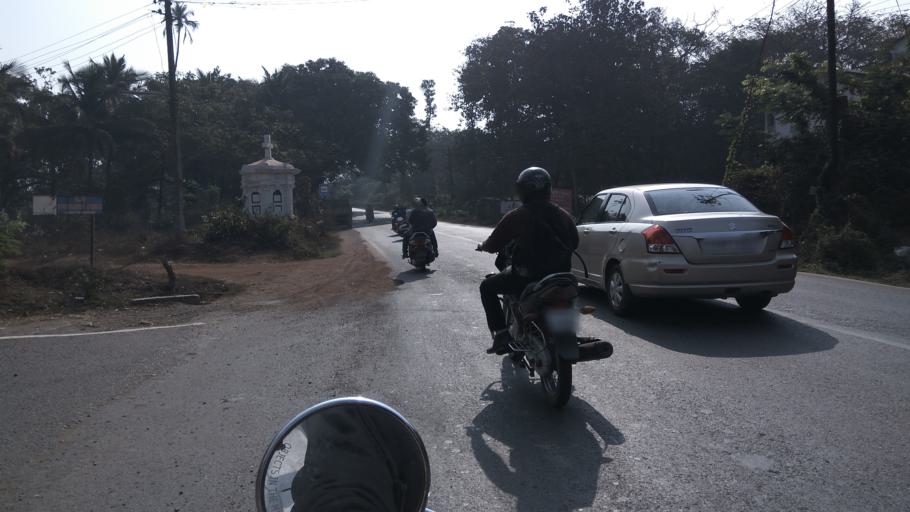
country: IN
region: Goa
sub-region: North Goa
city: Jua
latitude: 15.4981
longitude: 73.9222
